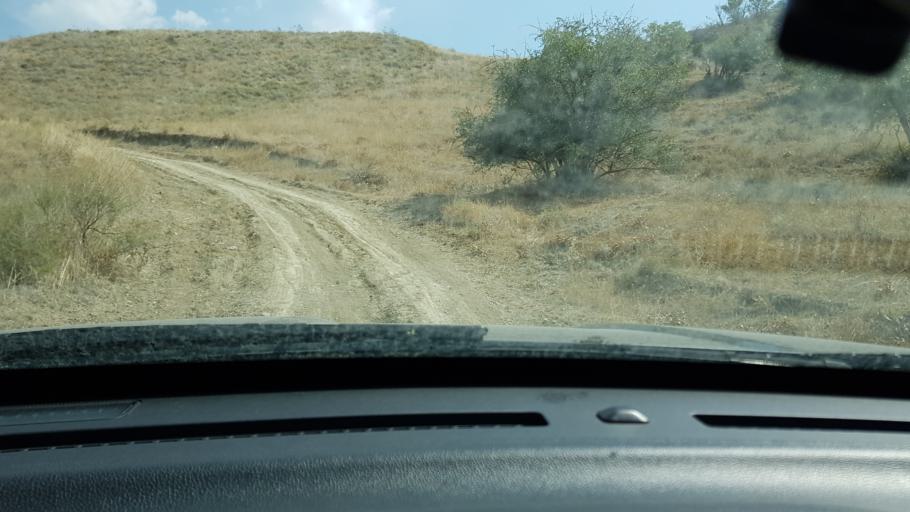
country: TM
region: Ahal
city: Baharly
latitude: 38.4050
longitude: 56.9076
